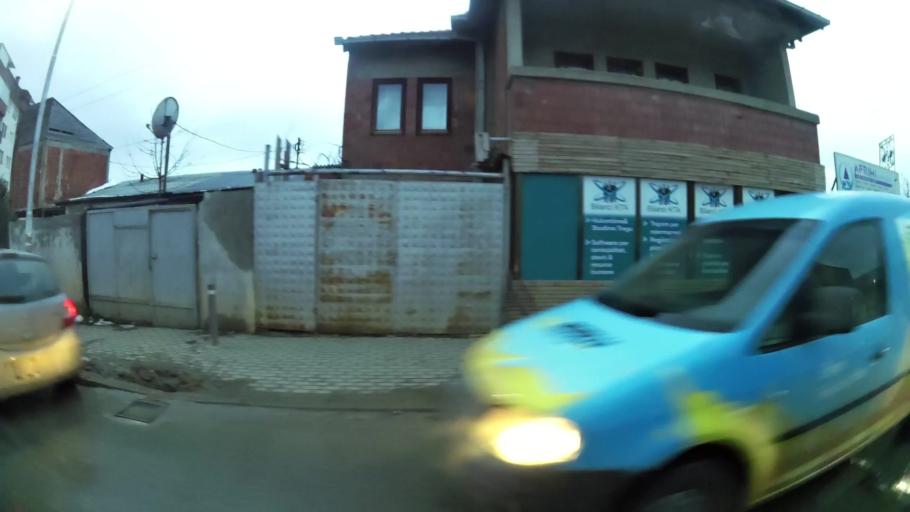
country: XK
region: Pristina
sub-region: Komuna e Prishtines
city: Pristina
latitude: 42.6440
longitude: 21.1672
